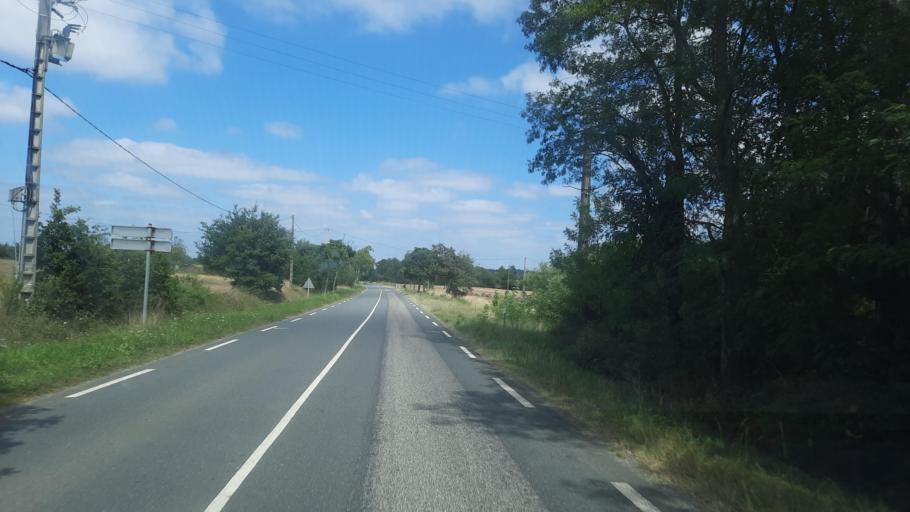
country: FR
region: Midi-Pyrenees
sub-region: Departement de la Haute-Garonne
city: Boulogne-sur-Gesse
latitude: 43.2958
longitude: 0.6670
